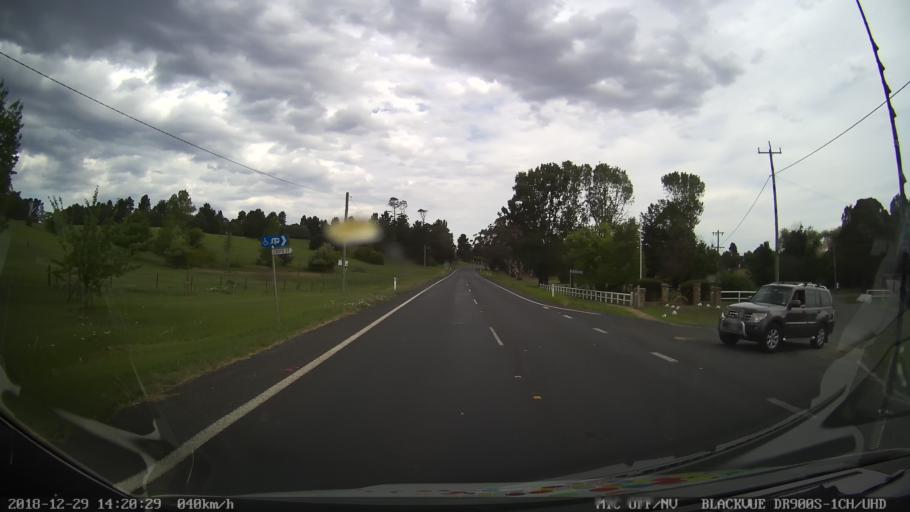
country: AU
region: New South Wales
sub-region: Cooma-Monaro
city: Cooma
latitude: -36.5082
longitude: 149.2854
